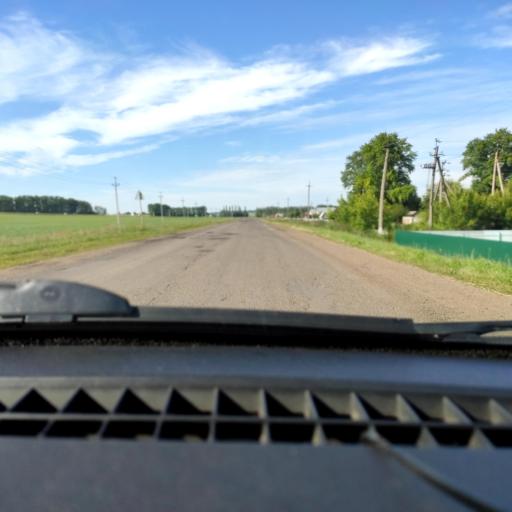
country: RU
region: Bashkortostan
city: Karmaskaly
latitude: 54.3960
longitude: 56.2447
